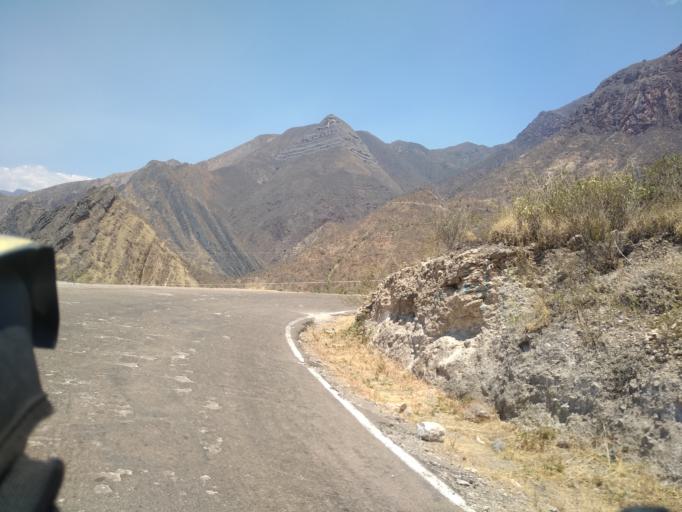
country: PE
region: Amazonas
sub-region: Provincia de Chachapoyas
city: Balsas
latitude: -6.8482
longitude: -78.0437
